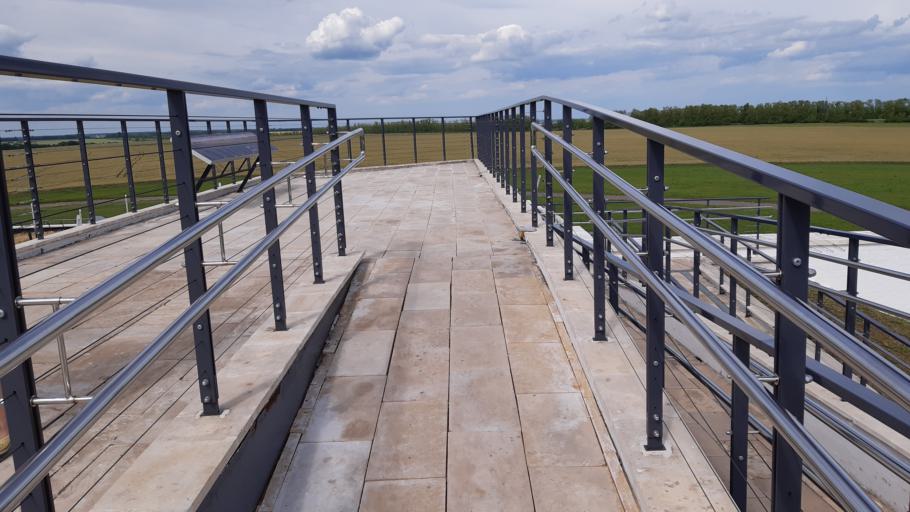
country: RU
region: Tula
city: Kurkino
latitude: 53.6248
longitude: 38.6725
